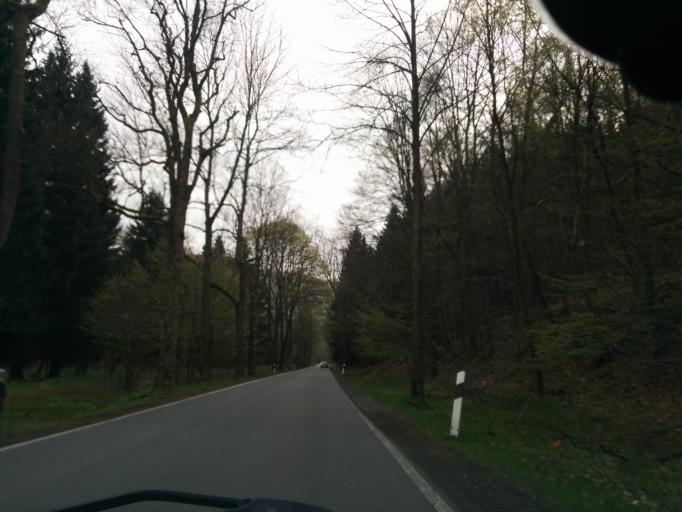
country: DE
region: Lower Saxony
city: Sankt Andreasberg
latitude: 51.6696
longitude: 10.5063
